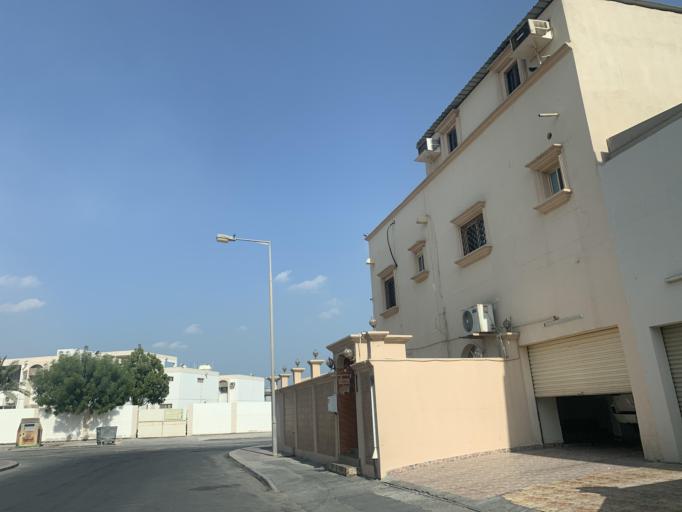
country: BH
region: Central Governorate
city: Madinat Hamad
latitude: 26.1263
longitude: 50.5043
